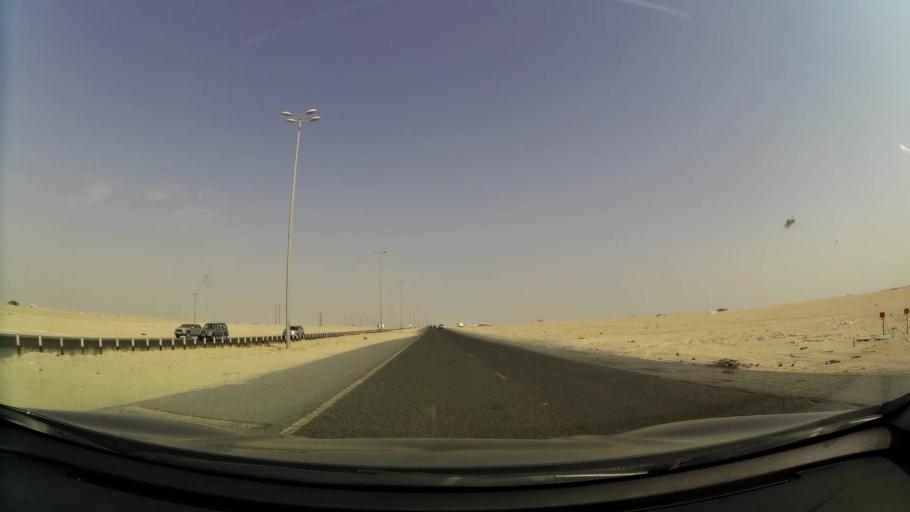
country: KW
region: Al Ahmadi
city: Al Wafrah
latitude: 28.8253
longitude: 48.0508
